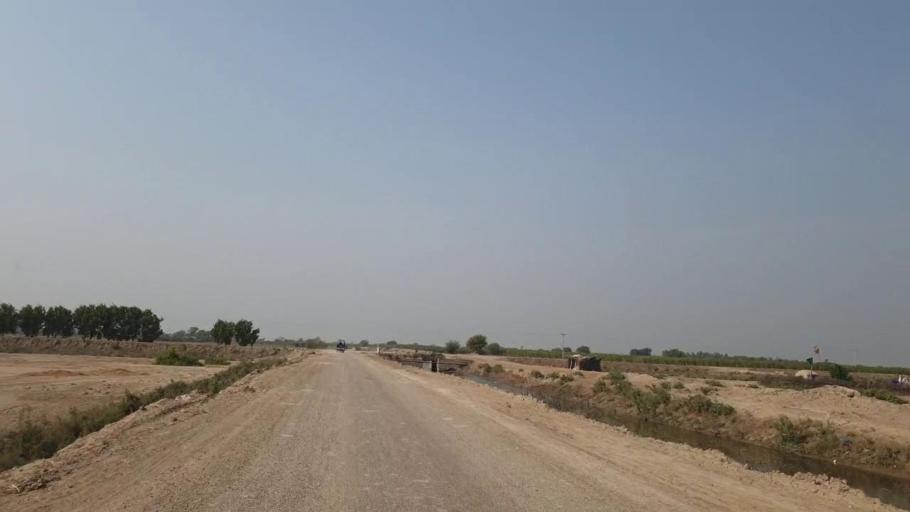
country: PK
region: Sindh
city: Tando Muhammad Khan
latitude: 24.9723
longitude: 68.5073
